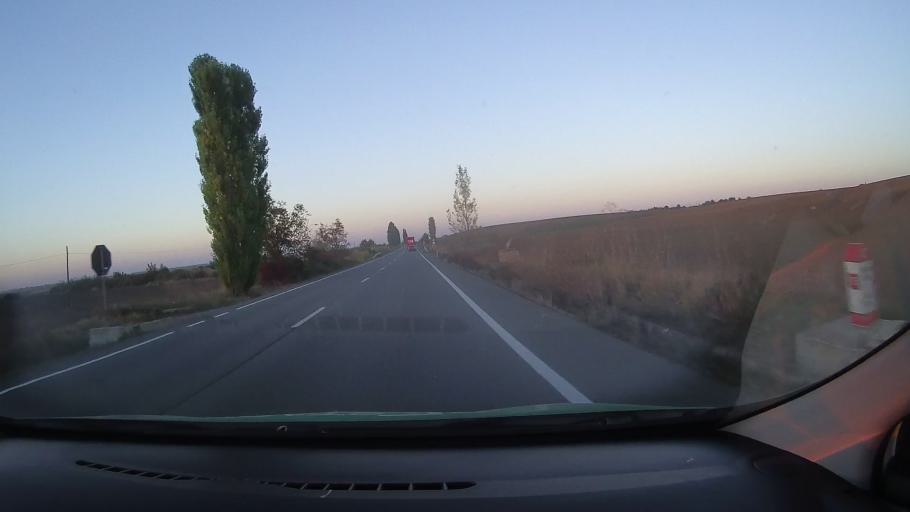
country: RO
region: Bihor
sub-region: Comuna Cherechiu
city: Cherechiu
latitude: 47.3873
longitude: 22.1454
